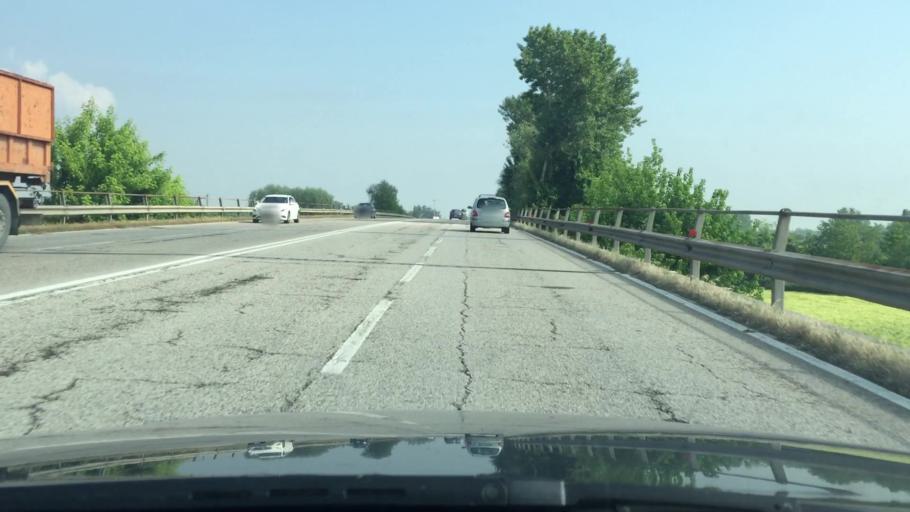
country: IT
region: Emilia-Romagna
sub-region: Provincia di Ferrara
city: Gaibanella-Sant'Edigio
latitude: 44.8005
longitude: 11.6367
